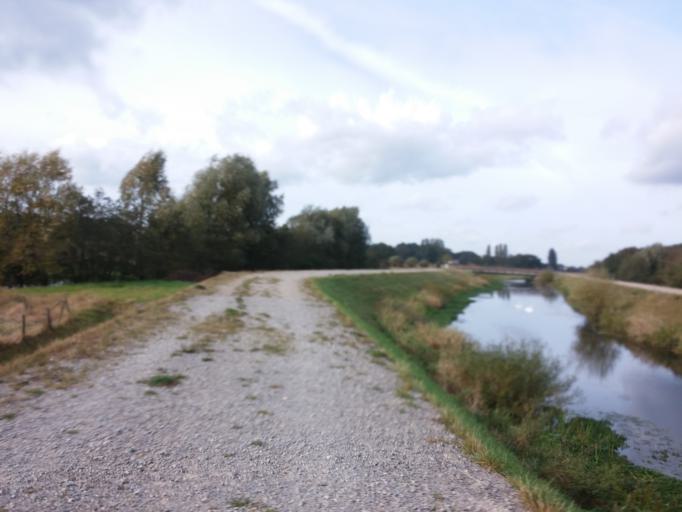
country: DE
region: North Rhine-Westphalia
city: Dorsten
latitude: 51.6460
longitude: 7.0053
